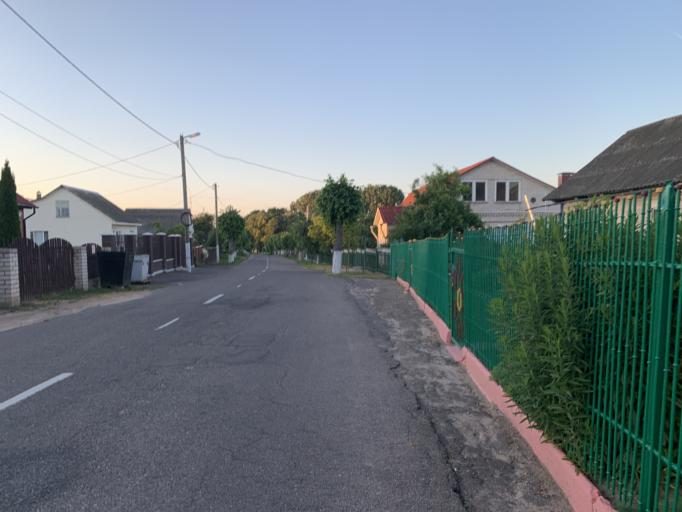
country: BY
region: Minsk
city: Nyasvizh
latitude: 53.2270
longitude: 26.6812
